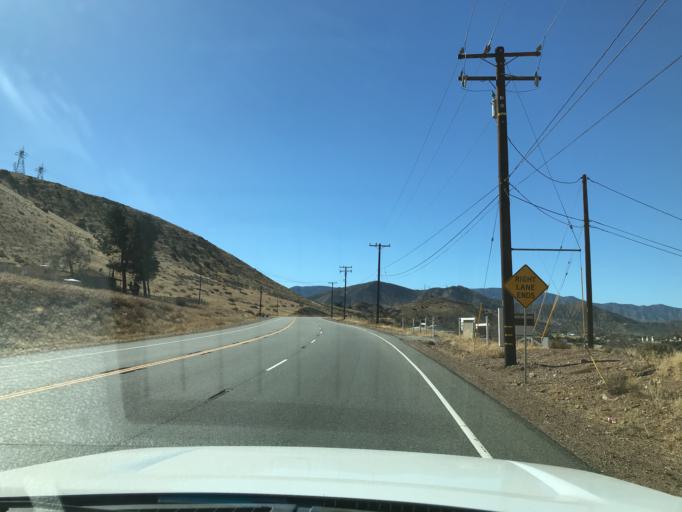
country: US
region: California
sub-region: Los Angeles County
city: Vincent
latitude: 34.5030
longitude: -118.1137
